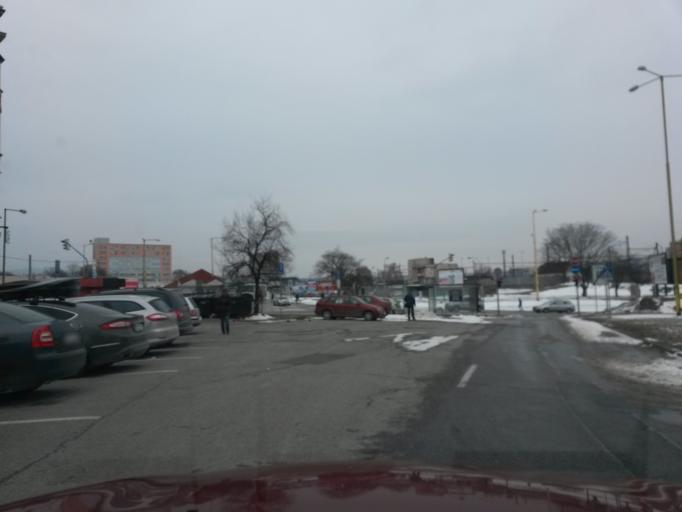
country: SK
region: Kosicky
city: Kosice
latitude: 48.7182
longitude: 21.2691
